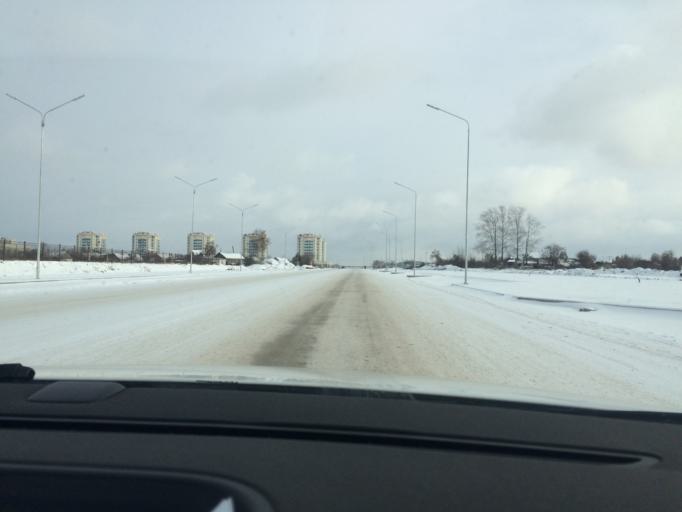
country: KZ
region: Astana Qalasy
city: Astana
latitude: 51.1206
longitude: 71.4951
